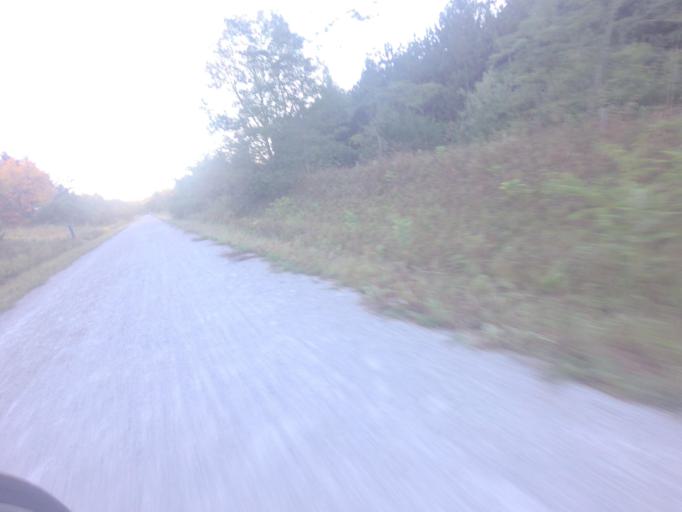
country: CA
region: Ontario
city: Bradford West Gwillimbury
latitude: 43.9626
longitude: -79.8252
